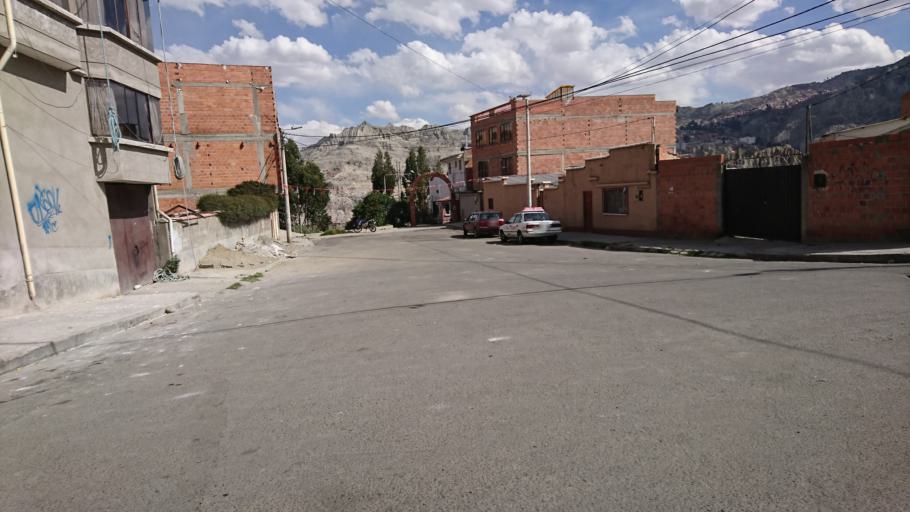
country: BO
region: La Paz
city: La Paz
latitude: -16.5158
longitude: -68.1137
